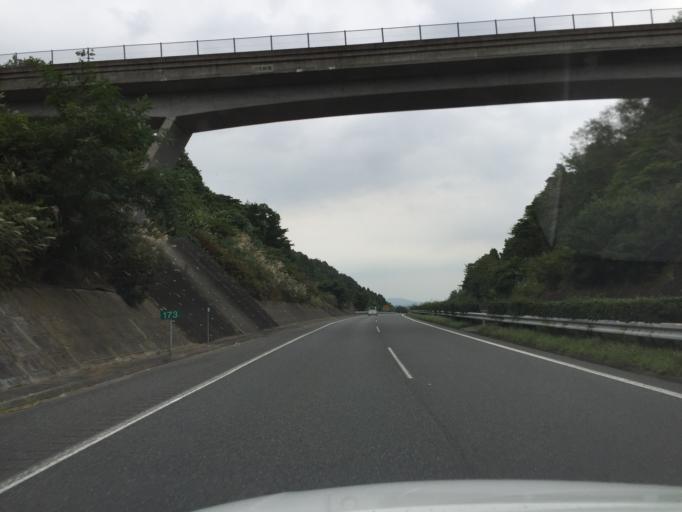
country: JP
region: Fukushima
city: Iwaki
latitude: 37.0523
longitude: 140.8237
